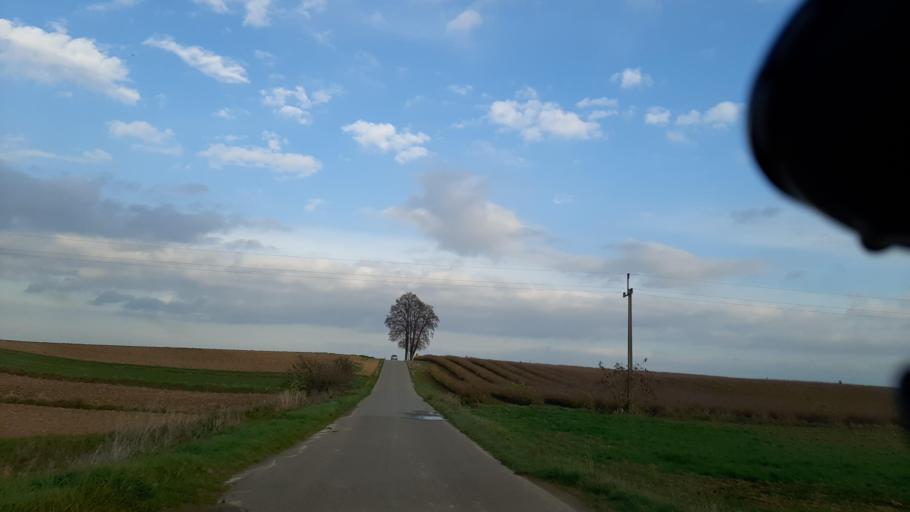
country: PL
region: Lublin Voivodeship
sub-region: Powiat pulawski
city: Markuszow
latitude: 51.3352
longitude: 22.2728
